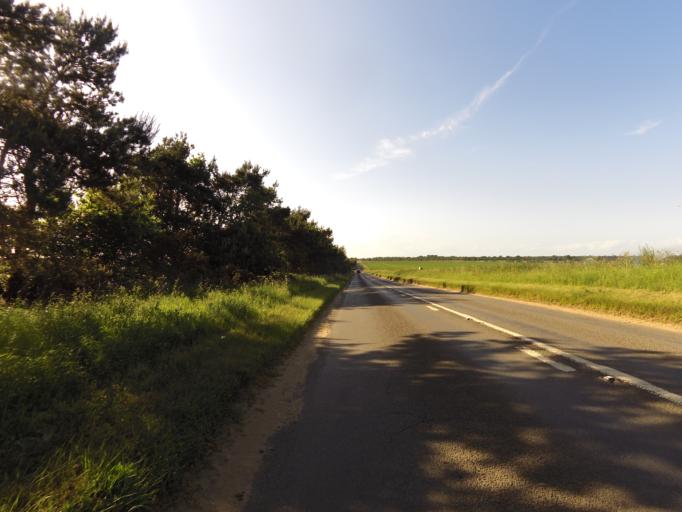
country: GB
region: England
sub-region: Suffolk
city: Woodbridge
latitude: 52.0796
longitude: 1.3623
